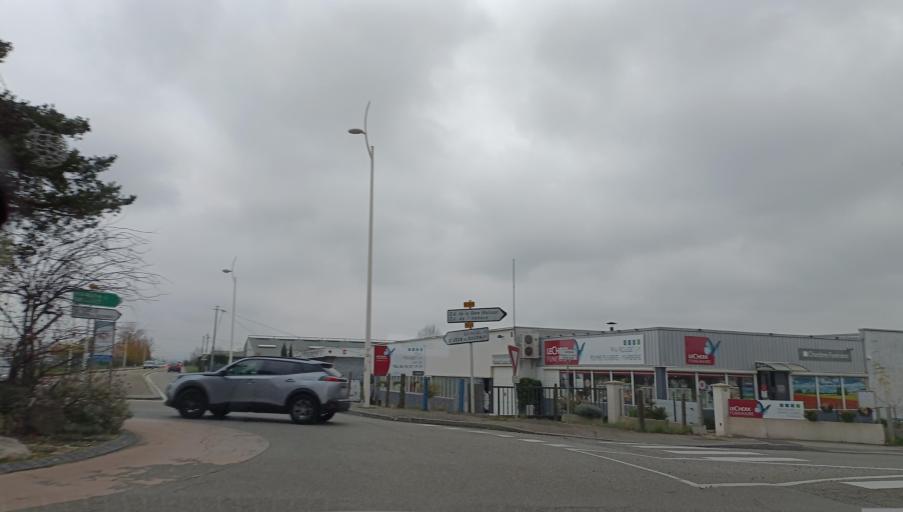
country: FR
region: Rhone-Alpes
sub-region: Departement de l'Isere
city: Pont-Eveque
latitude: 45.5245
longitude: 4.9199
